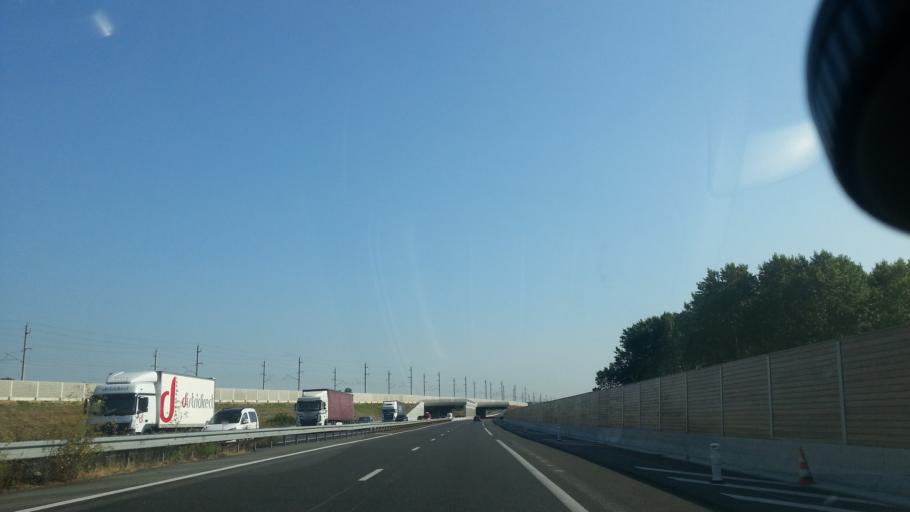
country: FR
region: Centre
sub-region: Departement d'Indre-et-Loire
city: La Celle-Saint-Avant
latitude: 47.0003
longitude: 0.5527
